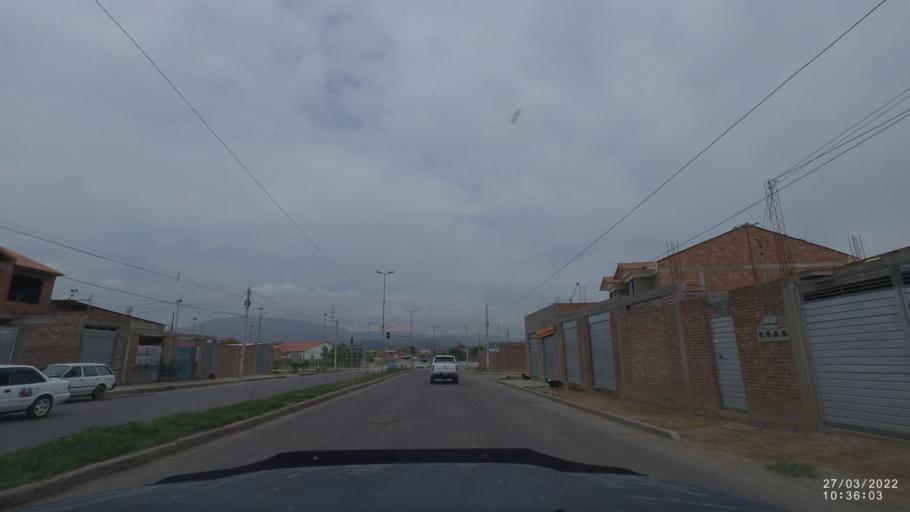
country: BO
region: Cochabamba
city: Cochabamba
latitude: -17.4415
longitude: -66.1522
